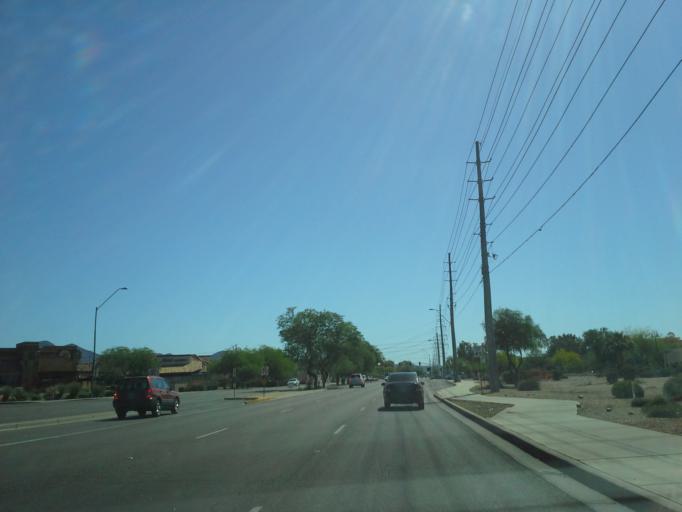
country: US
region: Arizona
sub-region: Maricopa County
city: Scottsdale
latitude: 33.5824
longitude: -111.8890
